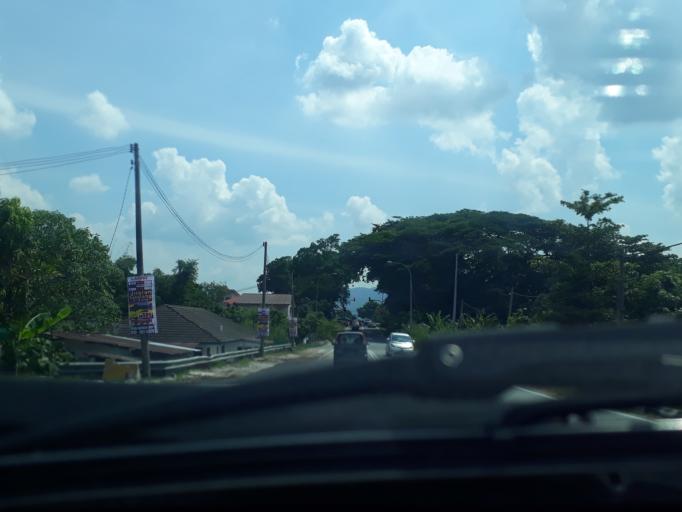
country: MY
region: Perak
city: Ipoh
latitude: 4.5774
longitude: 101.0889
